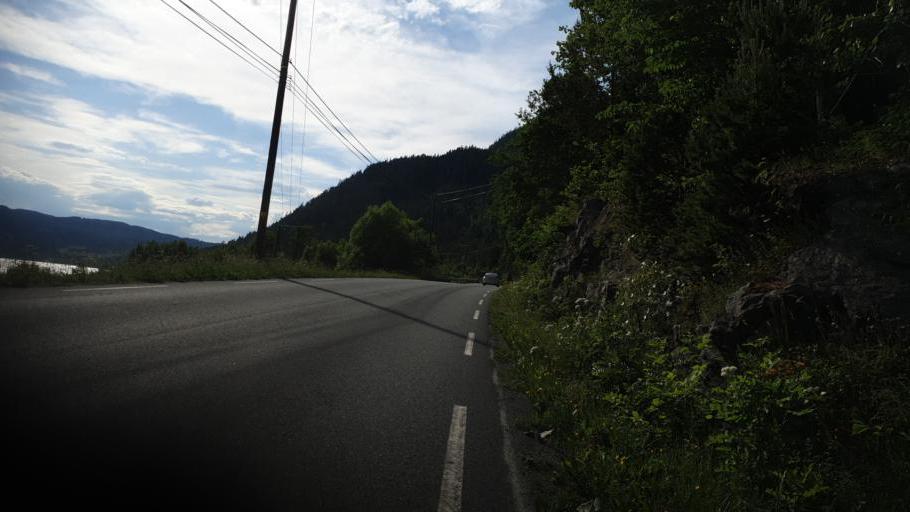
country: NO
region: Sor-Trondelag
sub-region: Trondheim
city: Trondheim
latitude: 63.5569
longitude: 10.2825
